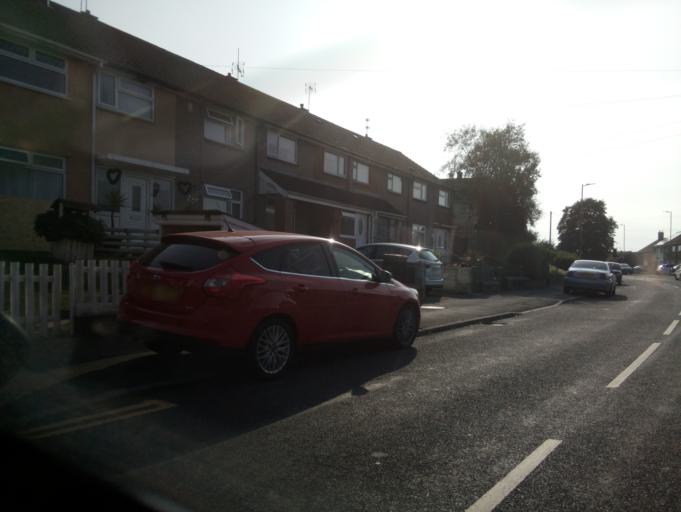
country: GB
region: Wales
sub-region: Newport
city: Newport
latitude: 51.6085
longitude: -3.0275
